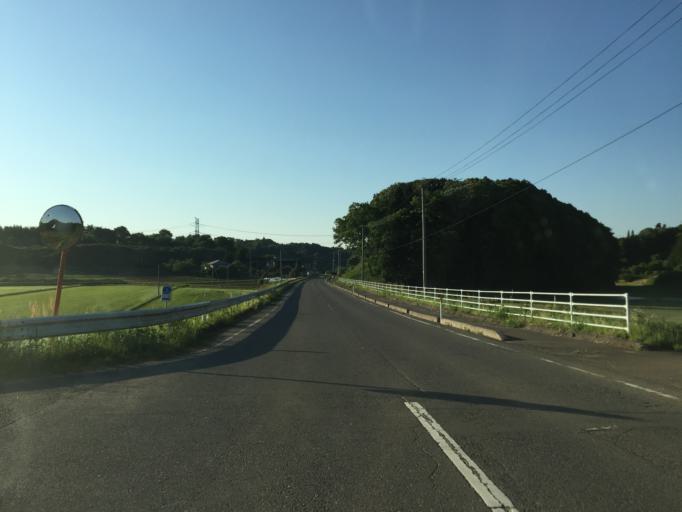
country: JP
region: Fukushima
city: Ishikawa
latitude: 37.0535
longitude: 140.4231
